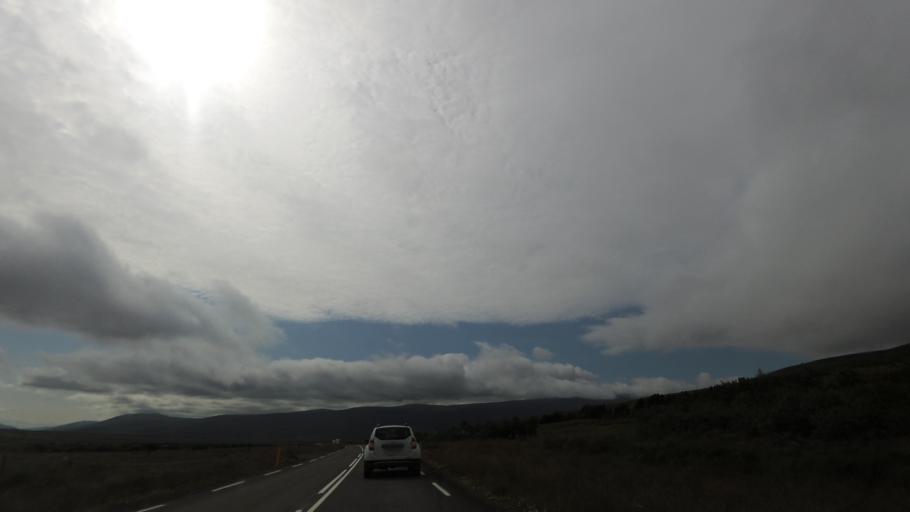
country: IS
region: Northeast
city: Laugar
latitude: 65.7247
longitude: -17.5964
